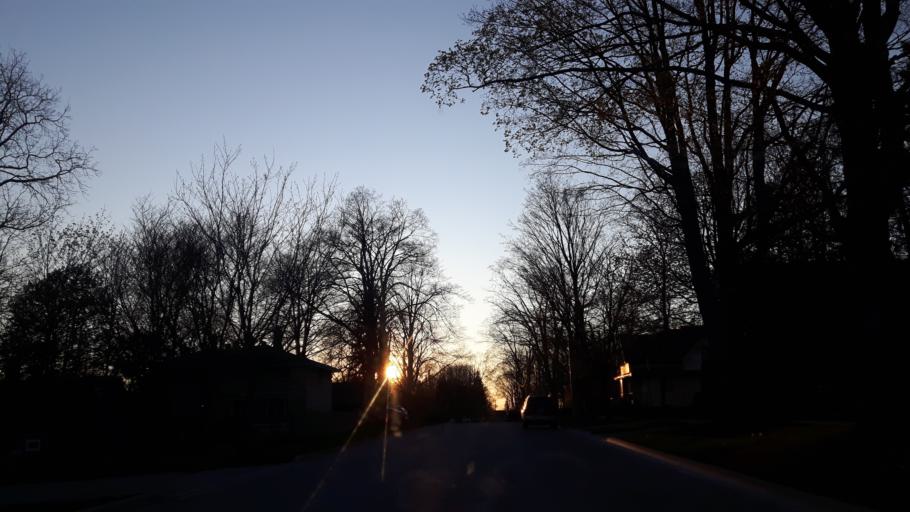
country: CA
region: Ontario
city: Bluewater
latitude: 43.6128
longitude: -81.5345
